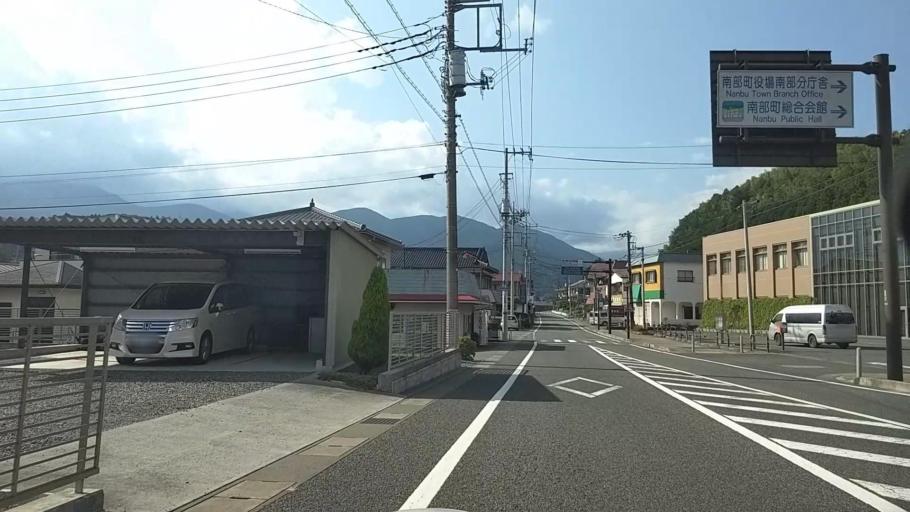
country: JP
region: Shizuoka
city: Fujinomiya
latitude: 35.2834
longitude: 138.4624
